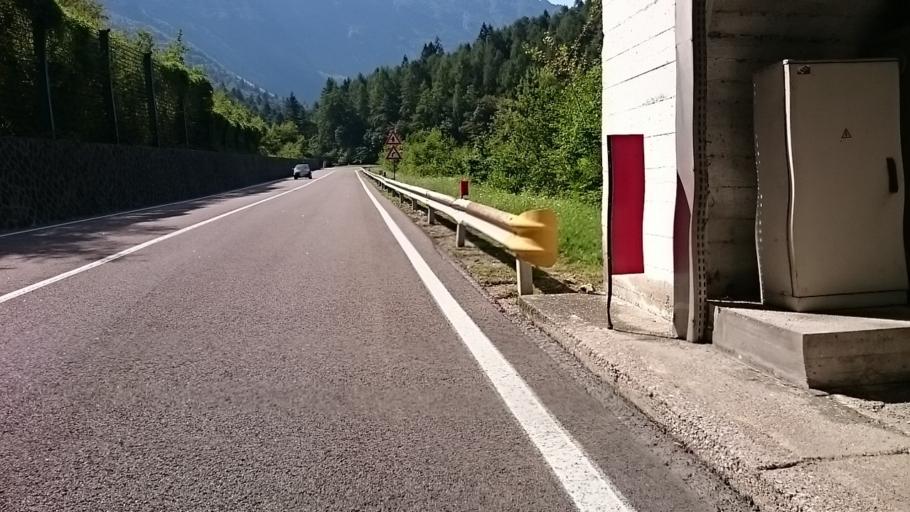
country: IT
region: Veneto
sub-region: Provincia di Belluno
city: Farra d'Alpago
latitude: 46.0907
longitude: 12.3425
